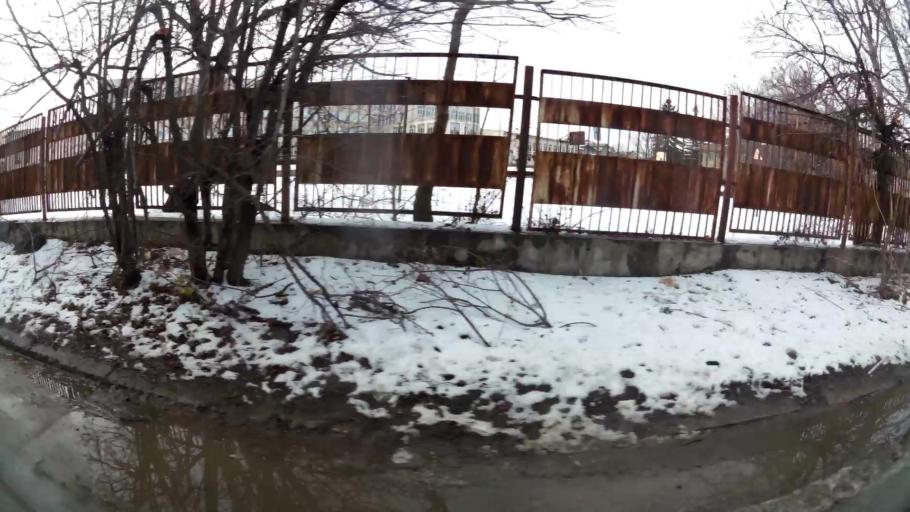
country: BG
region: Sofia-Capital
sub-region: Stolichna Obshtina
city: Sofia
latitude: 42.7160
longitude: 23.3478
